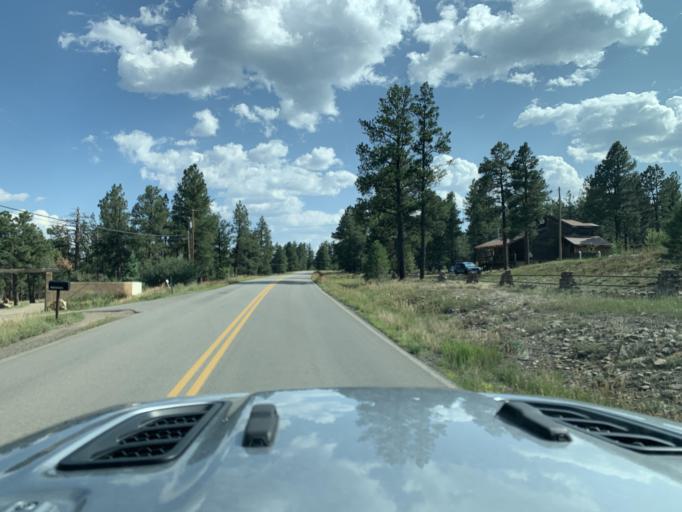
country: US
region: Colorado
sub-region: Archuleta County
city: Pagosa Springs
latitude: 37.2508
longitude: -107.0249
